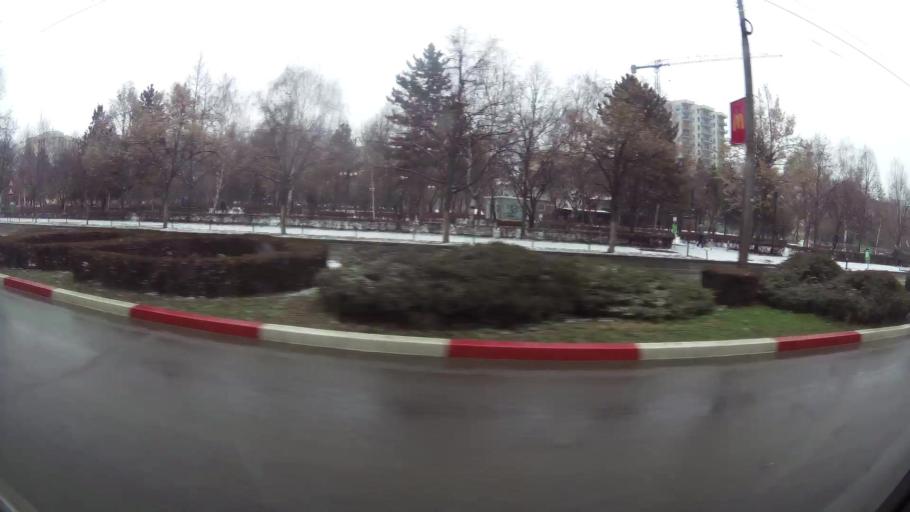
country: RO
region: Prahova
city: Ploiesti
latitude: 44.9457
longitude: 26.0136
